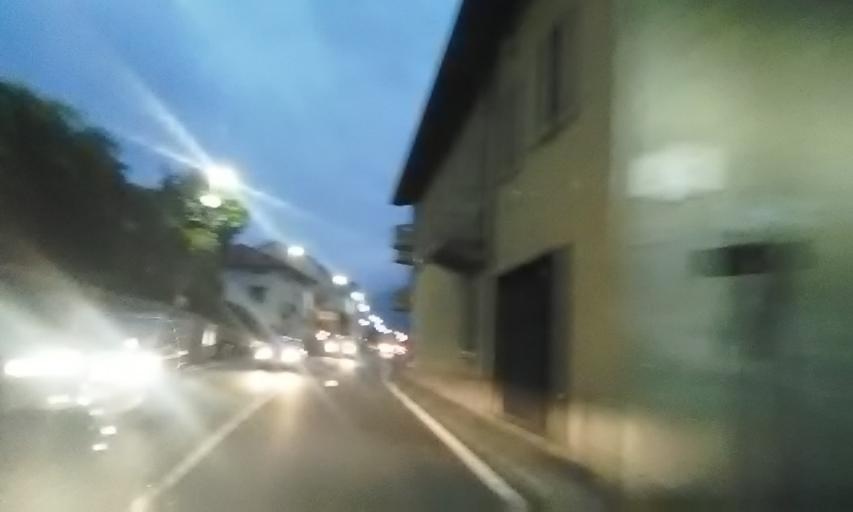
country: IT
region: Piedmont
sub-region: Provincia di Torino
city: Borgofranco d'Ivrea
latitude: 45.5126
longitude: 7.8556
